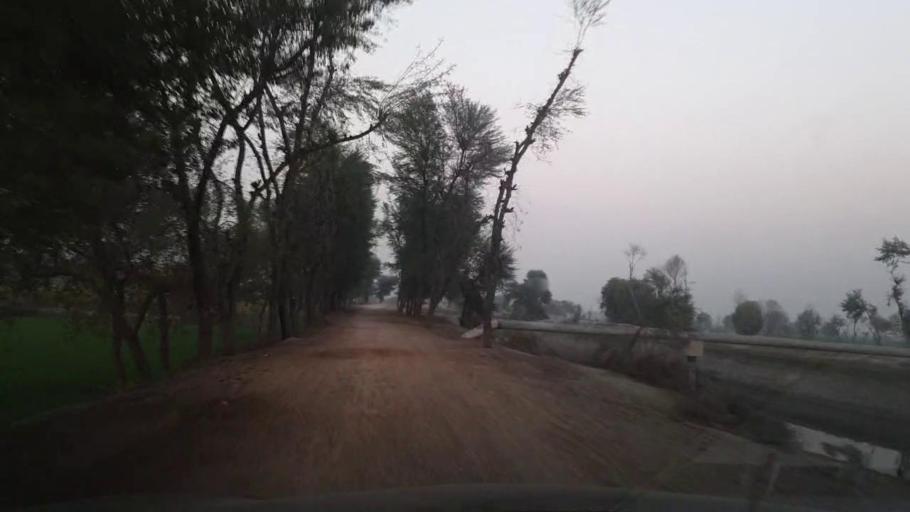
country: PK
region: Sindh
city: Ubauro
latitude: 28.1841
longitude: 69.7814
